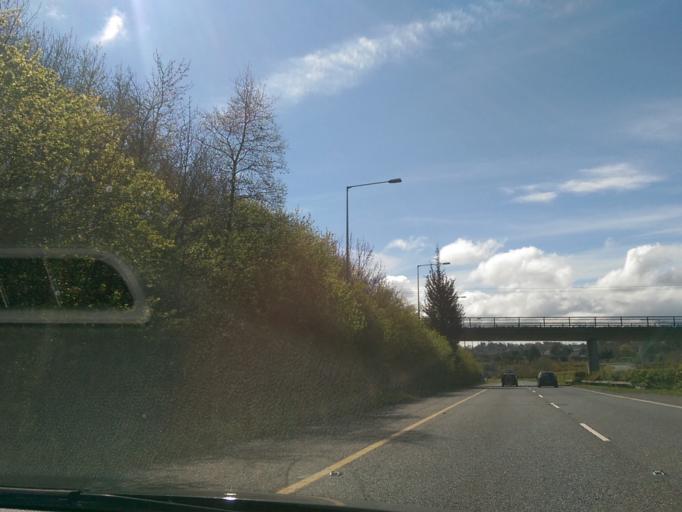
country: IE
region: Leinster
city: Loughlinstown
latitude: 53.2359
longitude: -6.1301
